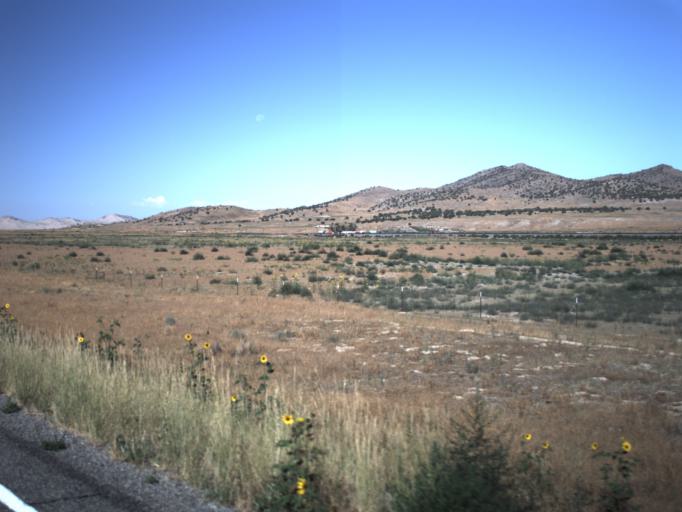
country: US
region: Utah
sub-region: Juab County
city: Nephi
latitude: 39.6782
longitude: -112.2556
